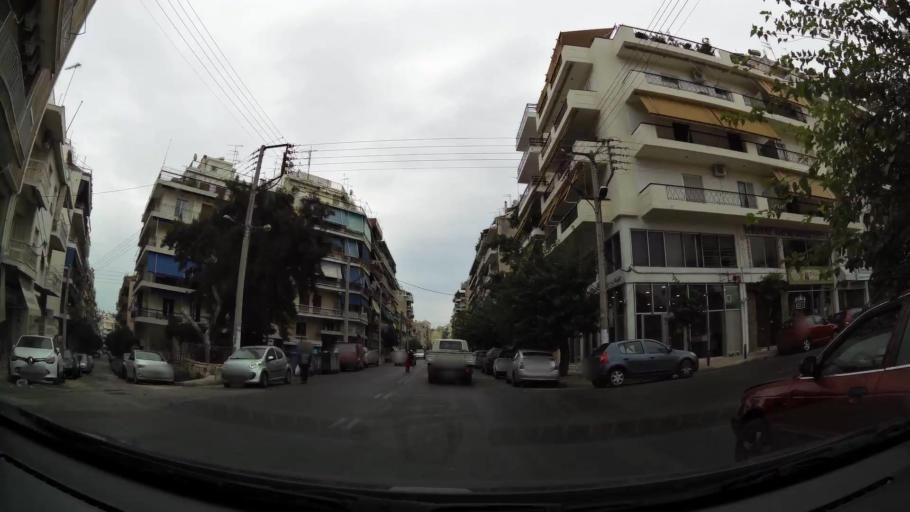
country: GR
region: Attica
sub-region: Nomos Attikis
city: Piraeus
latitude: 37.9341
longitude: 23.6417
